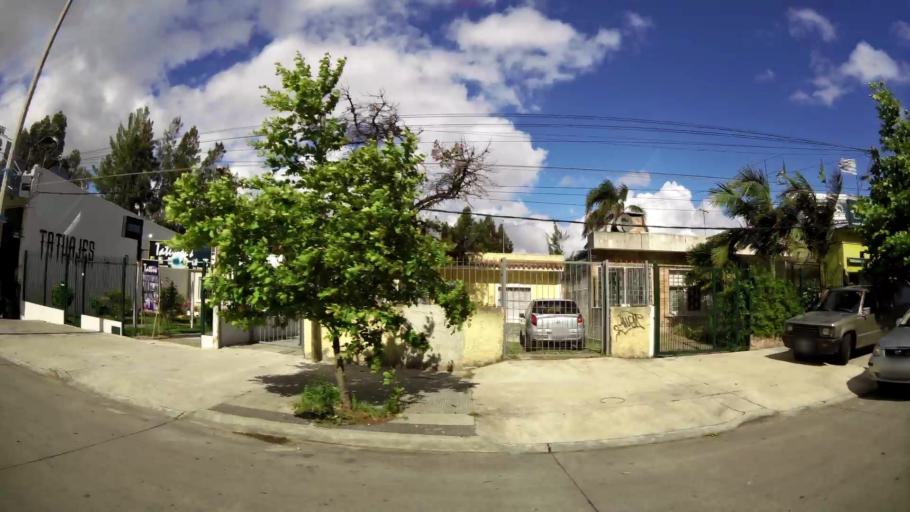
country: UY
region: Montevideo
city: Montevideo
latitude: -34.8404
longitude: -56.2216
